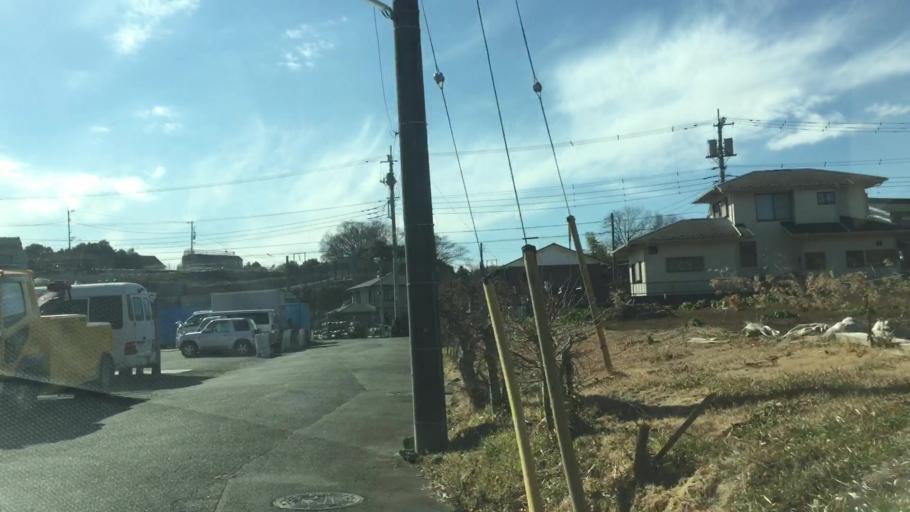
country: JP
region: Kanagawa
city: Yokohama
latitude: 35.4855
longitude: 139.5866
